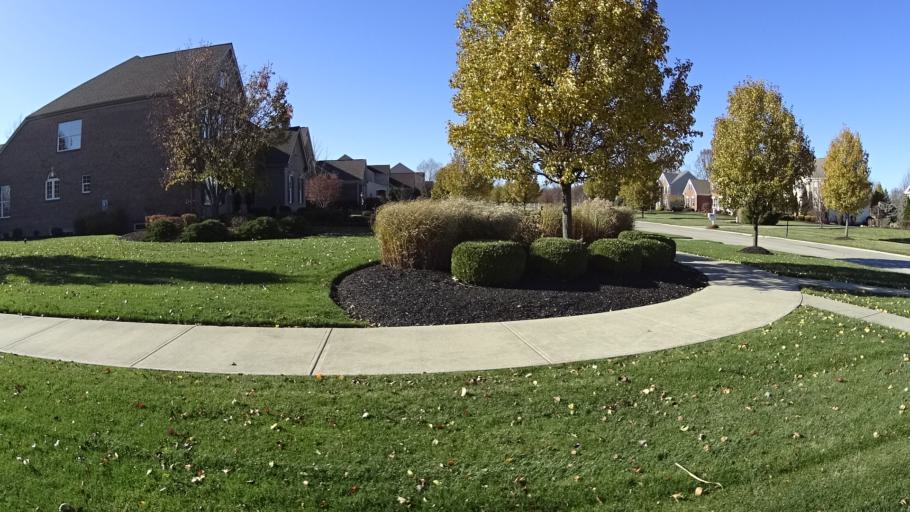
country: US
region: Ohio
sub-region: Lorain County
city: Avon
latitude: 41.4291
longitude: -82.0301
